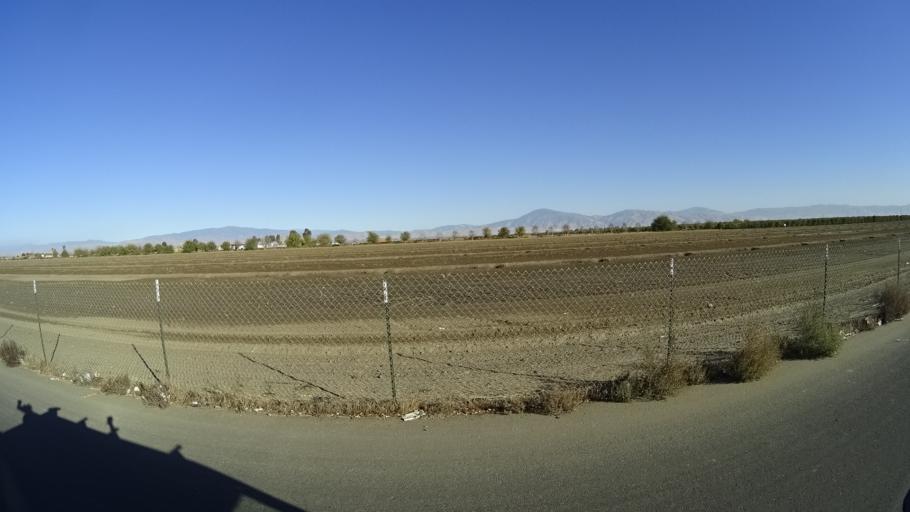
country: US
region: California
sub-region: Kern County
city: Greenfield
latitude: 35.2774
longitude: -118.9994
